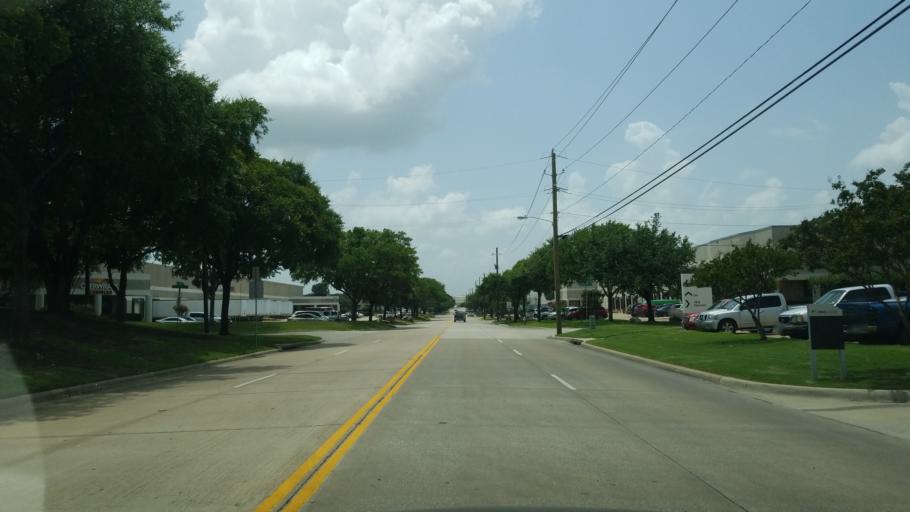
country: US
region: Texas
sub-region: Dallas County
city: Cockrell Hill
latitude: 32.7711
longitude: -96.8885
